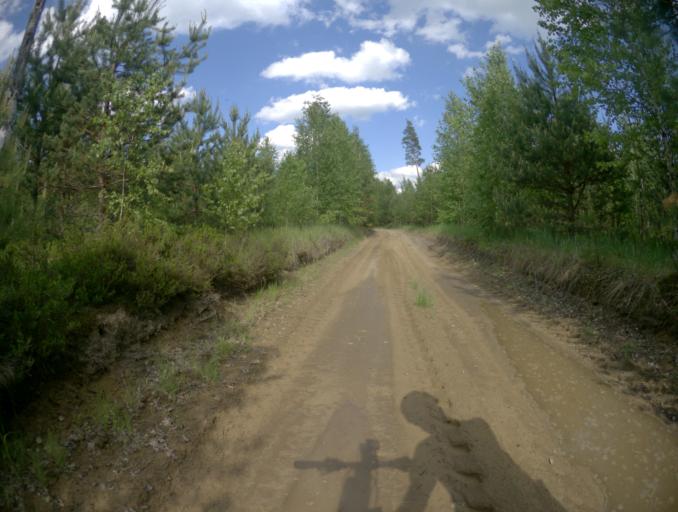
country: RU
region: Vladimir
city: Zolotkovo
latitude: 55.3303
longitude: 40.9811
